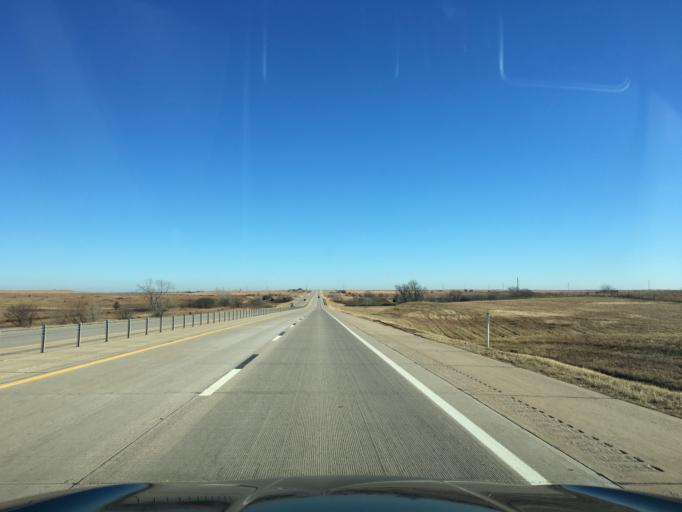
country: US
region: Oklahoma
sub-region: Noble County
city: Perry
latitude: 36.3920
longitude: -97.1475
